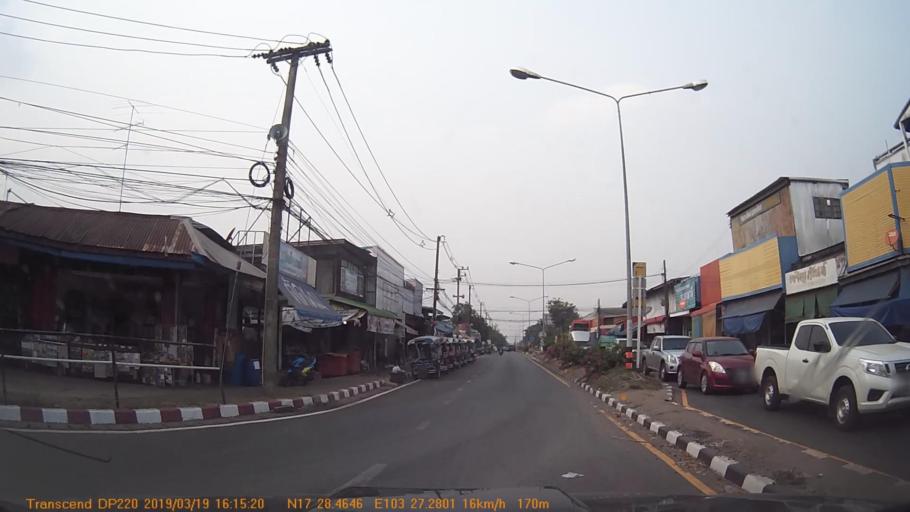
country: TH
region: Sakon Nakhon
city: Sawang Daen Din
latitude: 17.4745
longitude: 103.4548
